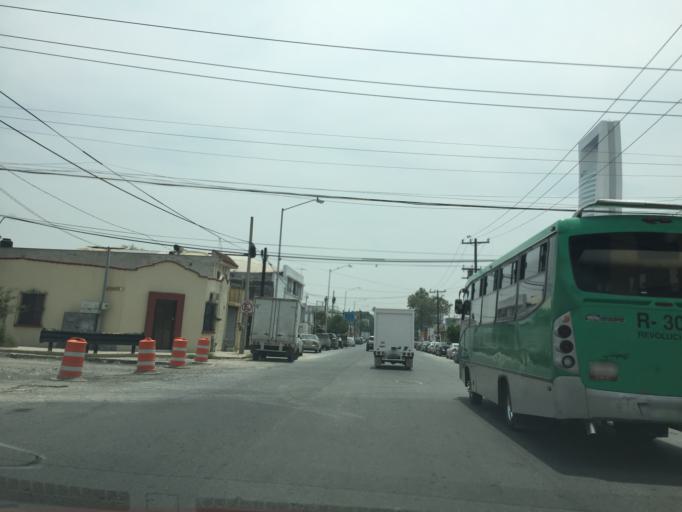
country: MX
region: Nuevo Leon
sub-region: Monterrey
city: Monterrey
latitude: 25.6778
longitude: -100.2969
